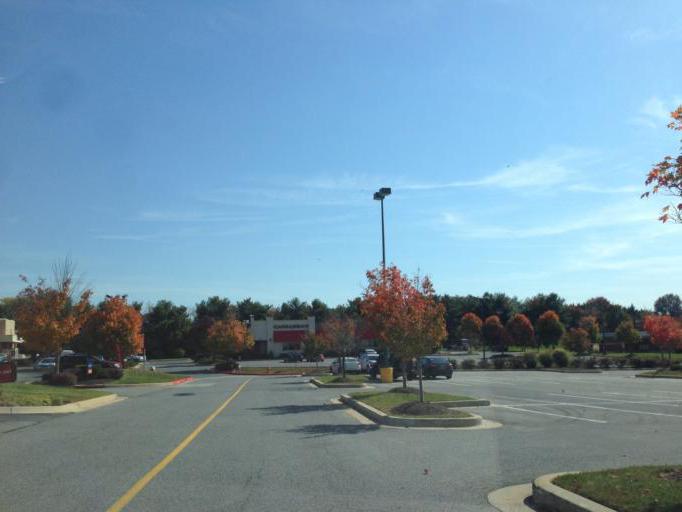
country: US
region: Maryland
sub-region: Howard County
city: Ellicott City
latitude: 39.2513
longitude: -76.8160
